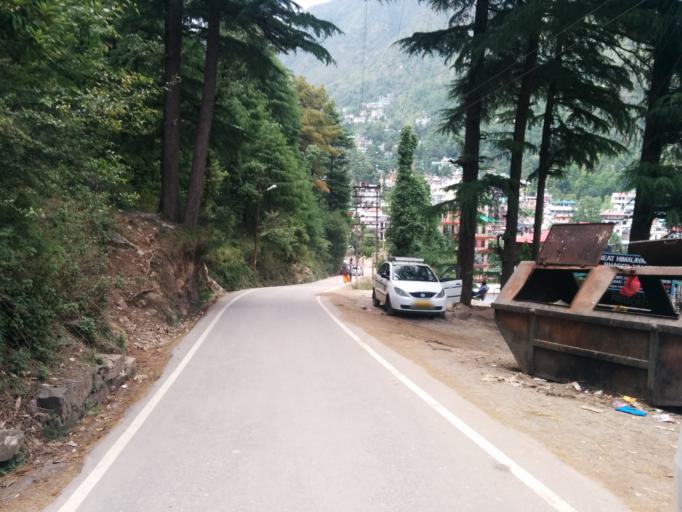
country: IN
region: Himachal Pradesh
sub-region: Kangra
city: Dharmsala
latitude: 32.2409
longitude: 76.3323
